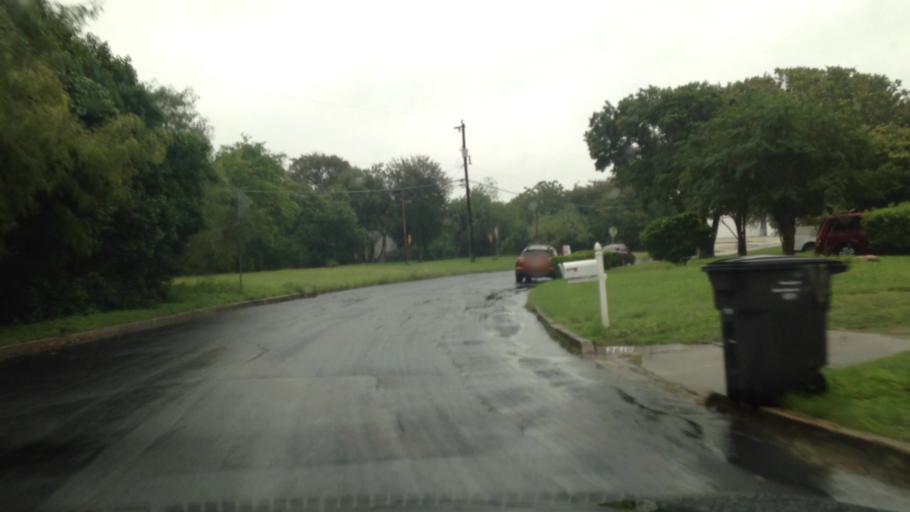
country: US
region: Texas
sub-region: Bexar County
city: Castle Hills
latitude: 29.5144
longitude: -98.5404
